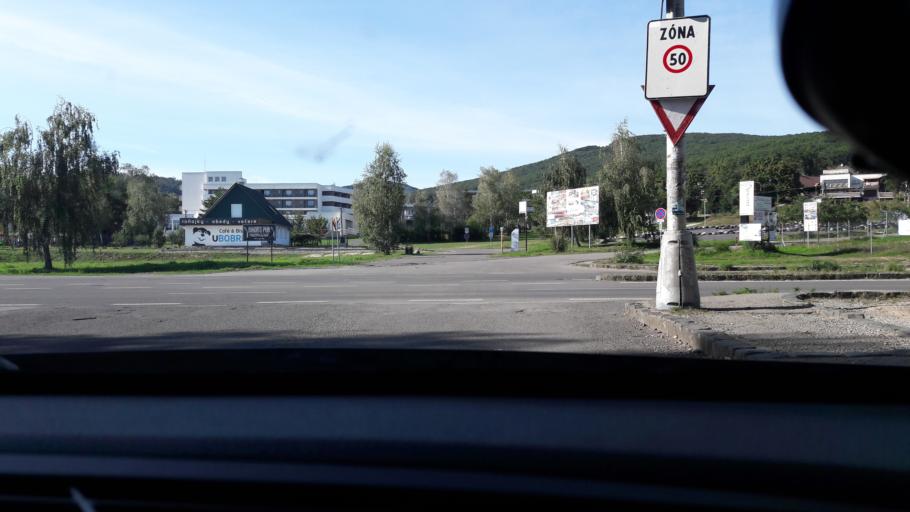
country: SK
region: Kosicky
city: Vinne
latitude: 48.8089
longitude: 22.0110
